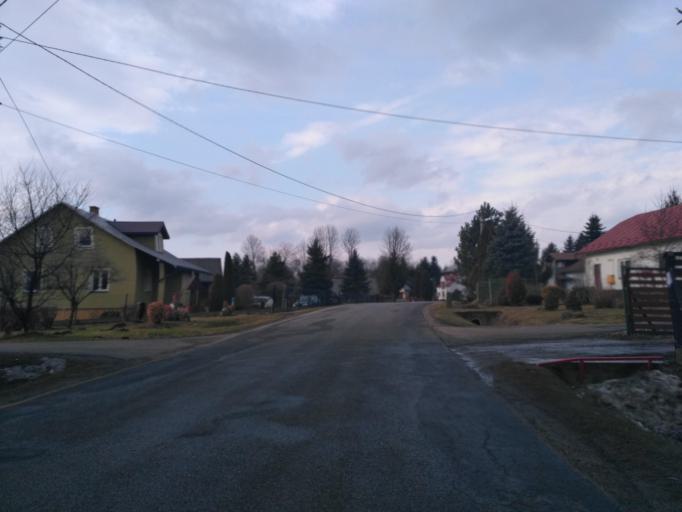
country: PL
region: Subcarpathian Voivodeship
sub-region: Powiat sanocki
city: Strachocina
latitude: 49.6083
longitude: 22.0918
